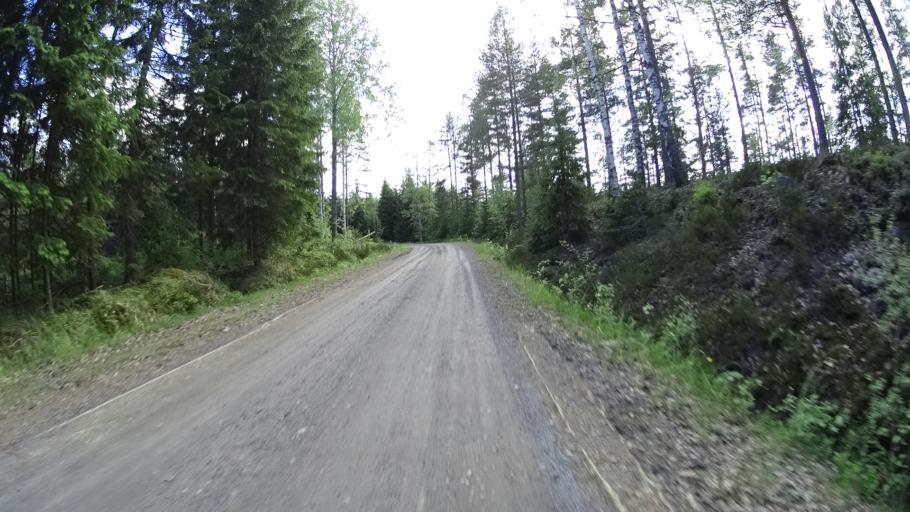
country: FI
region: Uusimaa
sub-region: Raaseporin
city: Pohja
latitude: 60.1573
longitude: 23.4890
